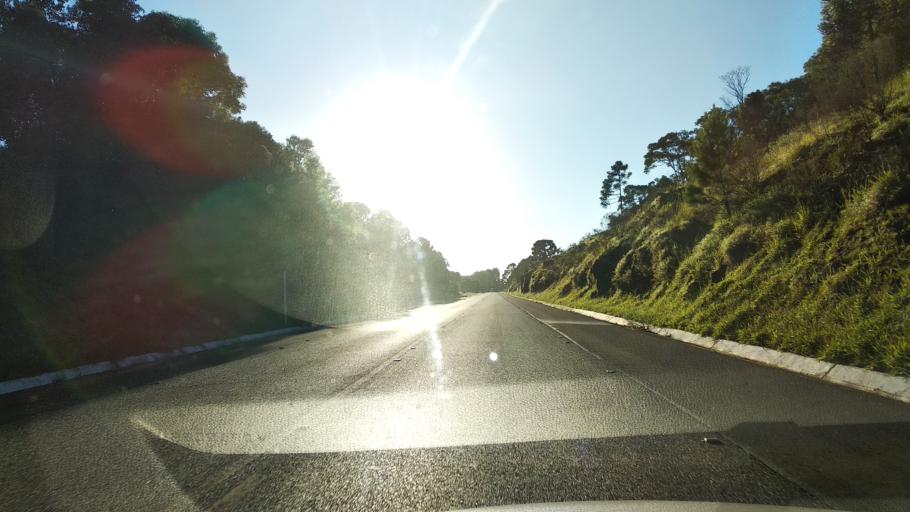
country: BR
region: Santa Catarina
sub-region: Correia Pinto
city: Correia Pinto
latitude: -27.6168
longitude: -50.6789
